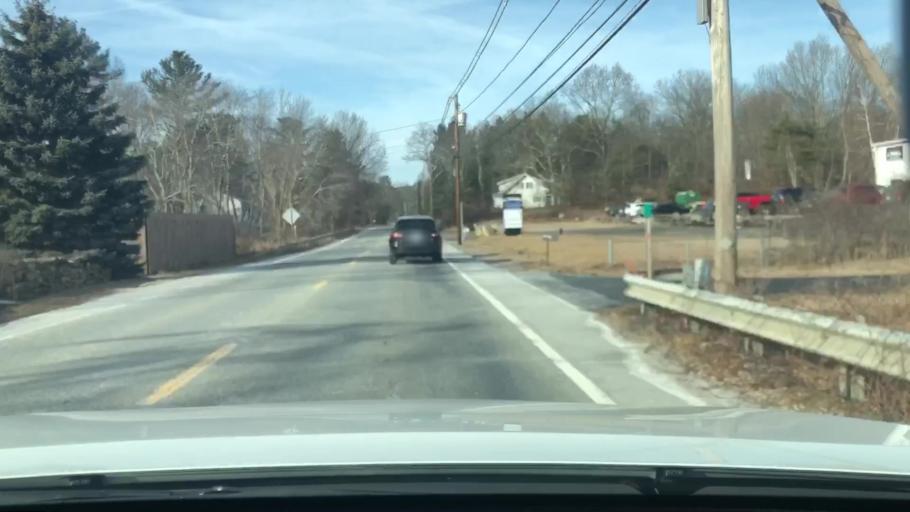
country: US
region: Massachusetts
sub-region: Worcester County
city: Northbridge
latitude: 42.1859
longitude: -71.6490
